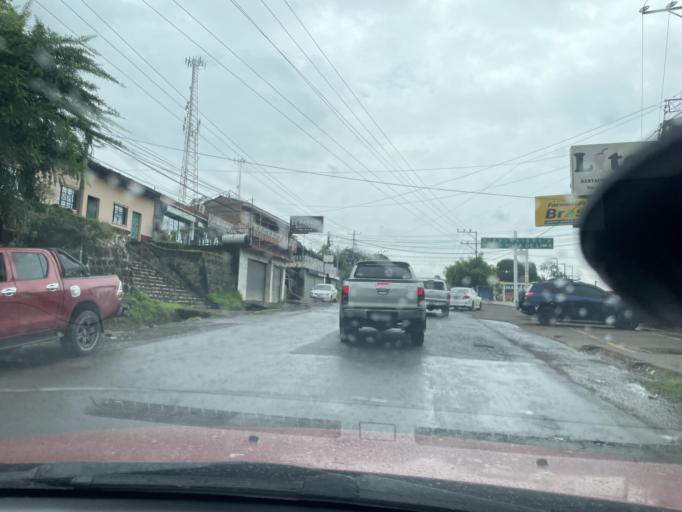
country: SV
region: La Union
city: Santa Rosa de Lima
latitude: 13.6241
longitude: -87.8937
